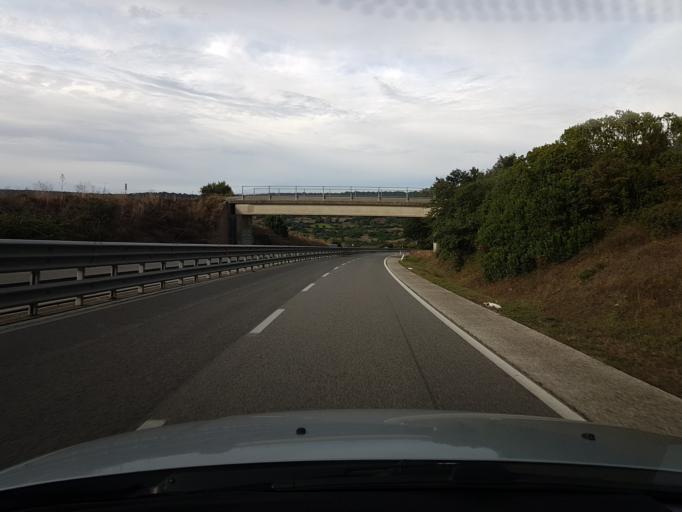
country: IT
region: Sardinia
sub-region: Provincia di Oristano
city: Soddi
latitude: 40.1425
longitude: 8.8735
